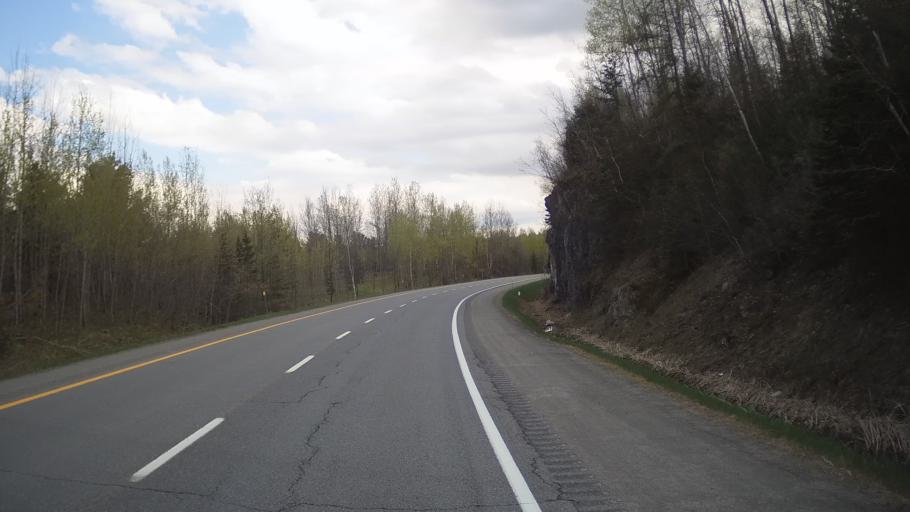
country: CA
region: Quebec
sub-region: Estrie
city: Magog
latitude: 45.1849
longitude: -72.0736
